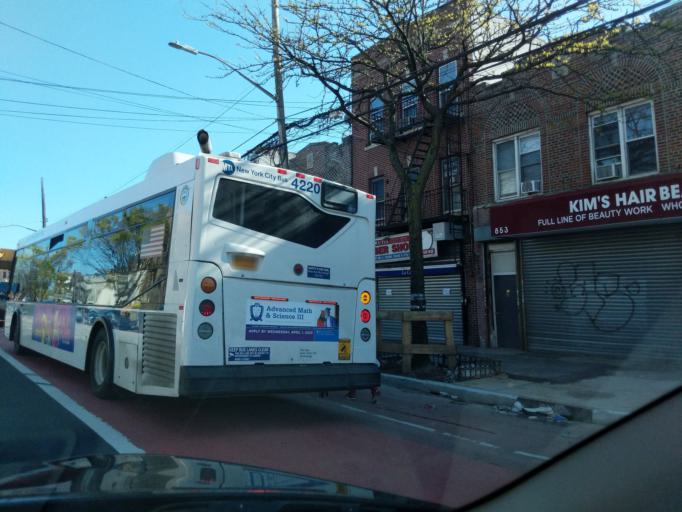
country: US
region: New York
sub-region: Kings County
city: Brooklyn
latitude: 40.6523
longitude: -73.9305
